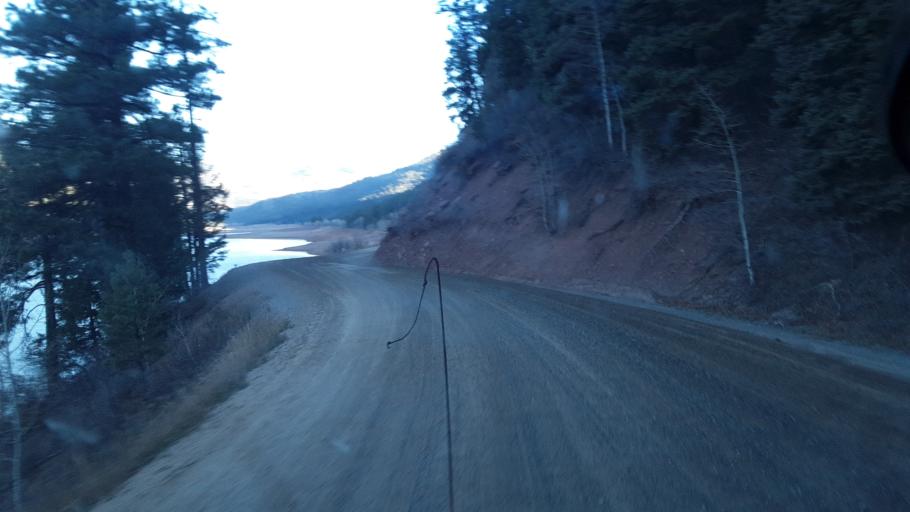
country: US
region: Colorado
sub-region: La Plata County
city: Bayfield
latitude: 37.3871
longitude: -107.6567
